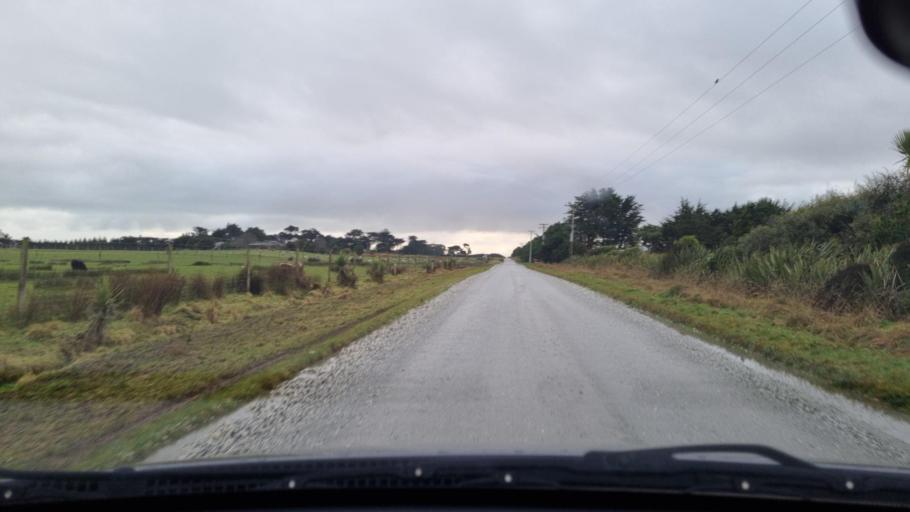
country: NZ
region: Southland
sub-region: Invercargill City
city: Invercargill
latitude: -46.4211
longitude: 168.2743
